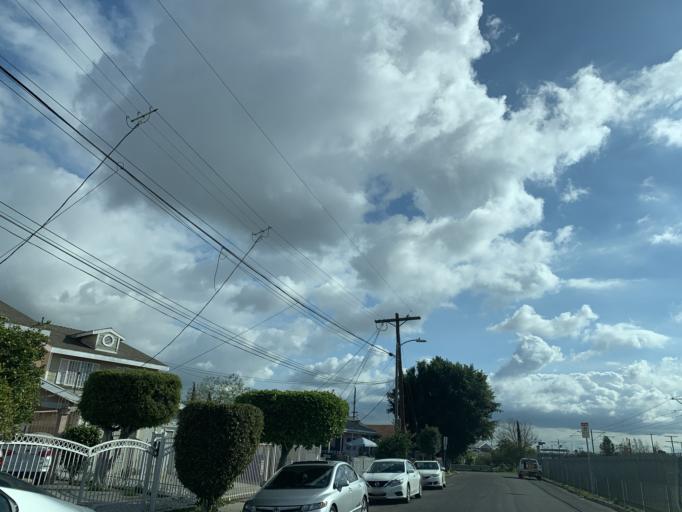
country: US
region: California
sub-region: Los Angeles County
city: Willowbrook
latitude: 33.9341
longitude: -118.2406
